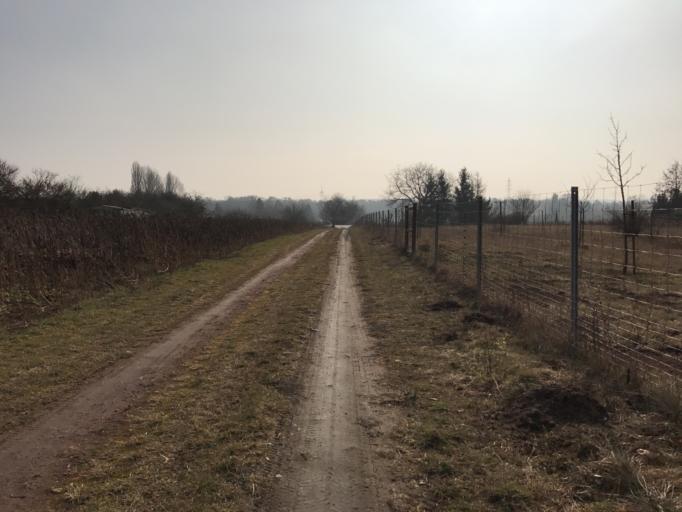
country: DE
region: Rheinland-Pfalz
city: Budenheim
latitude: 50.0216
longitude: 8.1511
